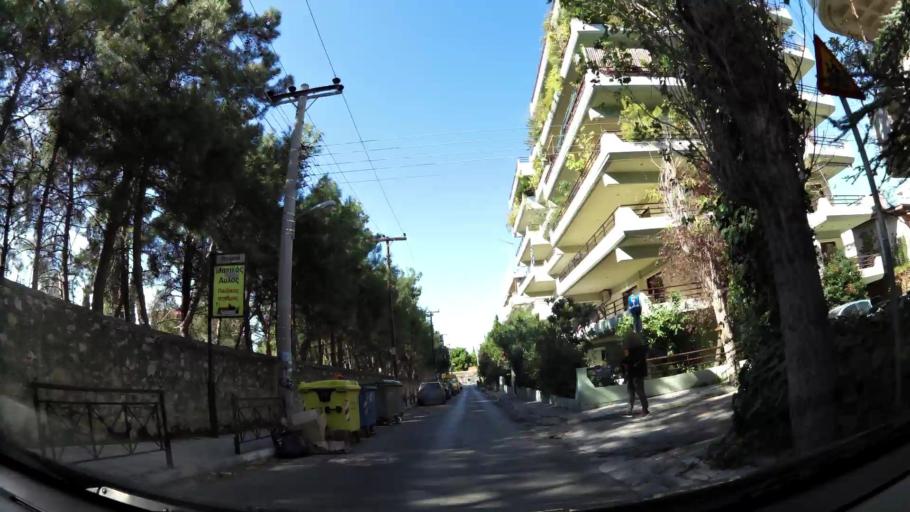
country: GR
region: Attica
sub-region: Nomarchia Athinas
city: Khalandrion
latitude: 38.0311
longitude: 23.8002
